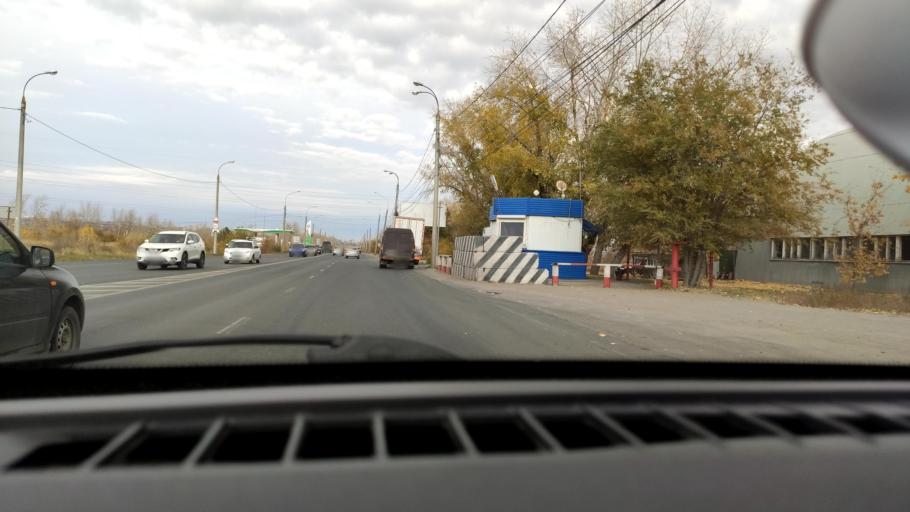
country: RU
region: Samara
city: Samara
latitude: 53.1433
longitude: 50.1812
